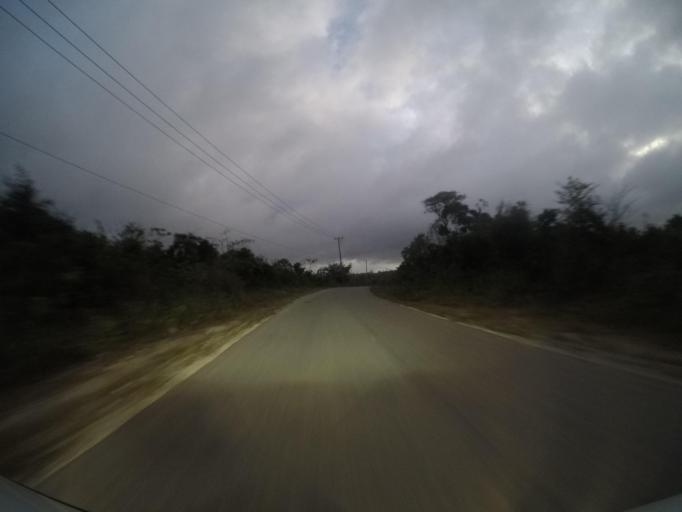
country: TL
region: Lautem
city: Lospalos
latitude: -8.3992
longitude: 127.0059
